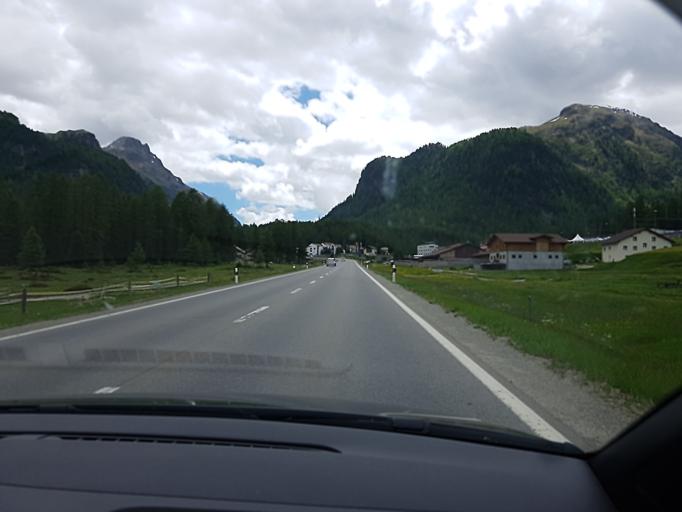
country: CH
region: Grisons
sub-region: Maloja District
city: Pontresina
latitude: 46.4947
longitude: 9.8941
